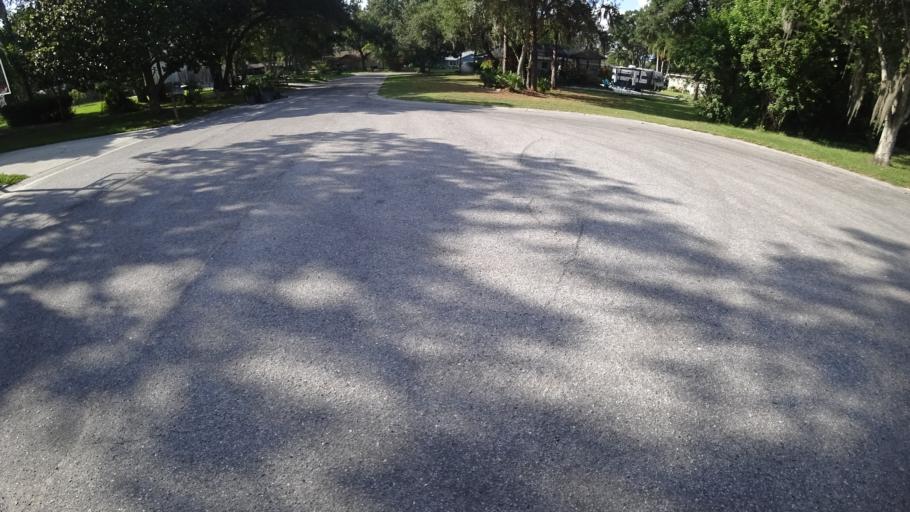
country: US
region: Florida
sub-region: Sarasota County
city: Desoto Lakes
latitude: 27.4330
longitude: -82.4530
